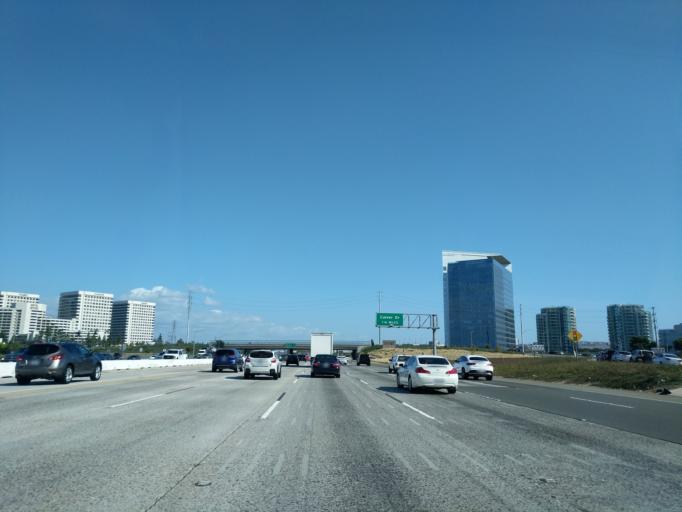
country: US
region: California
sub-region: Orange County
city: Irvine
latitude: 33.6780
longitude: -117.8466
